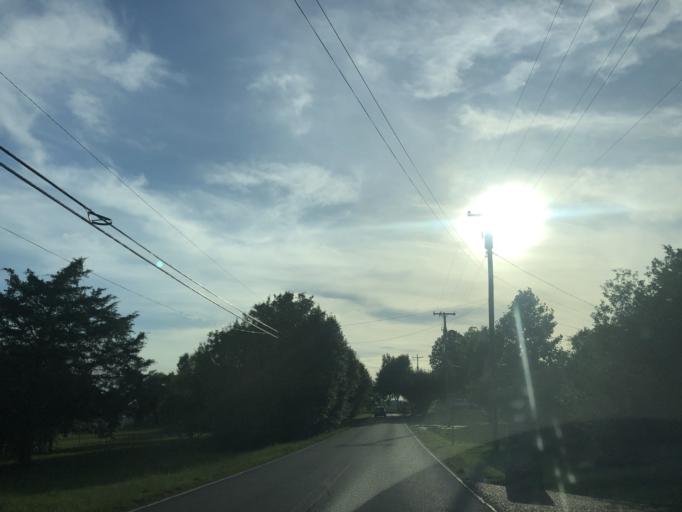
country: US
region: Tennessee
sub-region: Davidson County
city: Nashville
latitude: 36.2165
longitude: -86.8589
